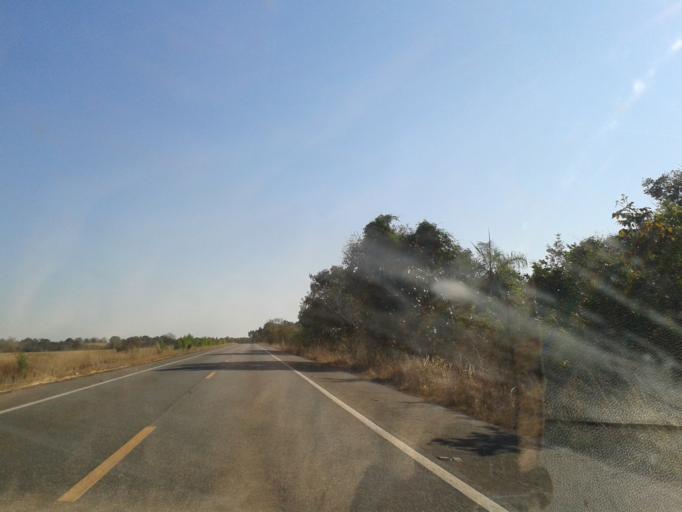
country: BR
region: Goias
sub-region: Mozarlandia
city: Mozarlandia
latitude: -14.9020
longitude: -50.5486
